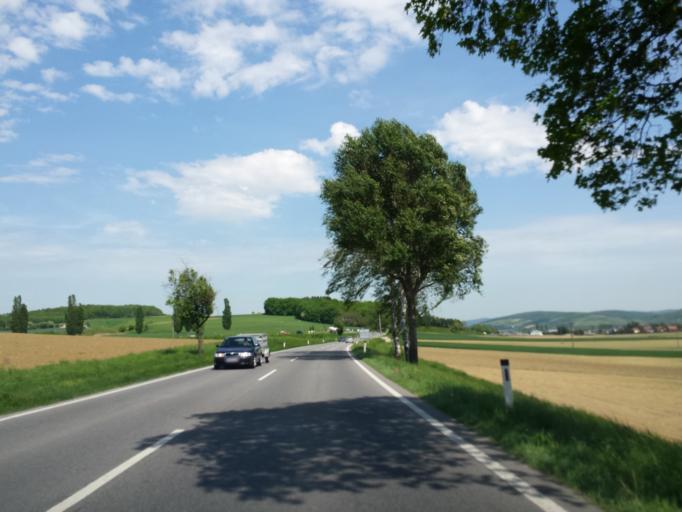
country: AT
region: Lower Austria
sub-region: Politischer Bezirk Tulln
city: Michelhausen
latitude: 48.2695
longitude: 15.9545
